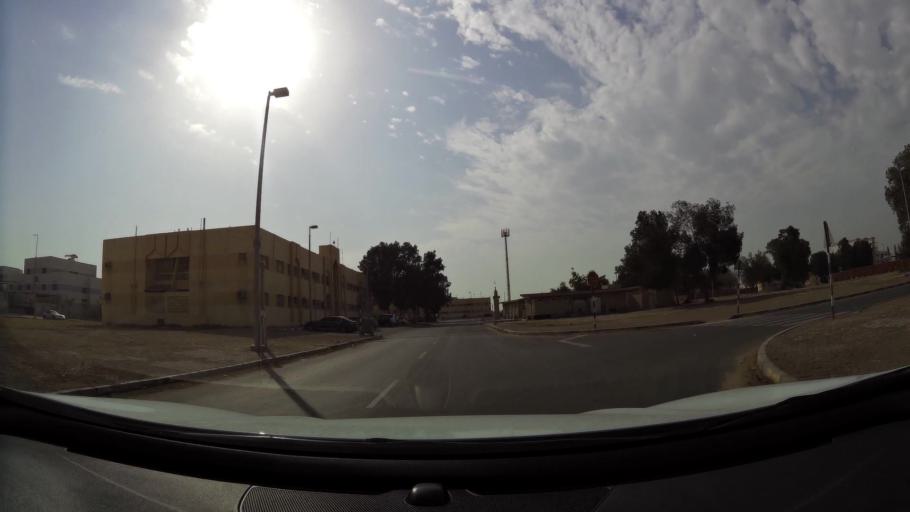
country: AE
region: Abu Dhabi
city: Abu Dhabi
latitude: 24.3177
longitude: 54.5328
